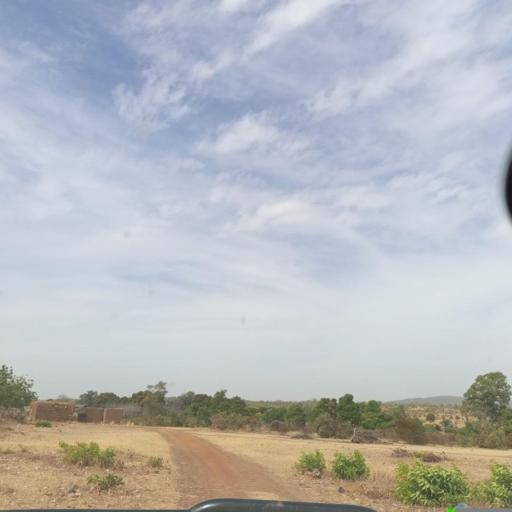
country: ML
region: Koulikoro
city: Koulikoro
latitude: 13.1656
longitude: -7.7284
